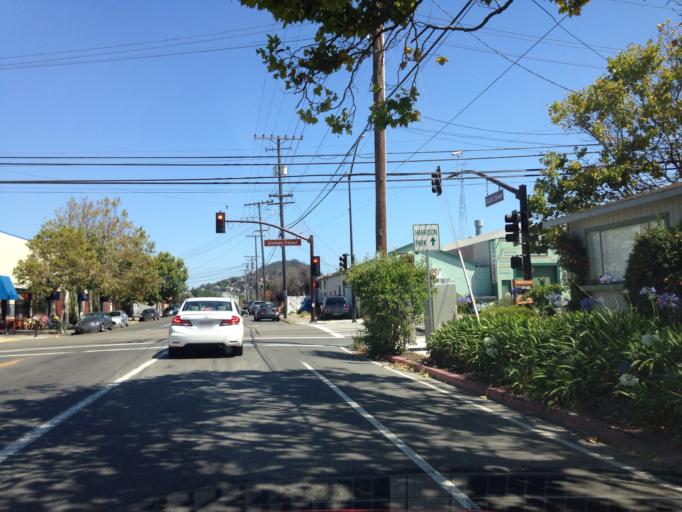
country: US
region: California
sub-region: Alameda County
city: Albany
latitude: 37.8791
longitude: -122.3012
